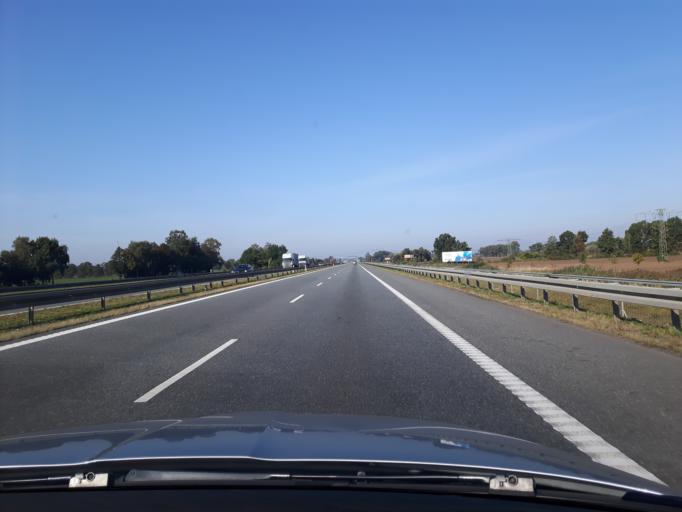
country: PL
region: Pomeranian Voivodeship
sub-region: Powiat gdanski
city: Cedry Wielkie
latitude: 54.3096
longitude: 18.7770
